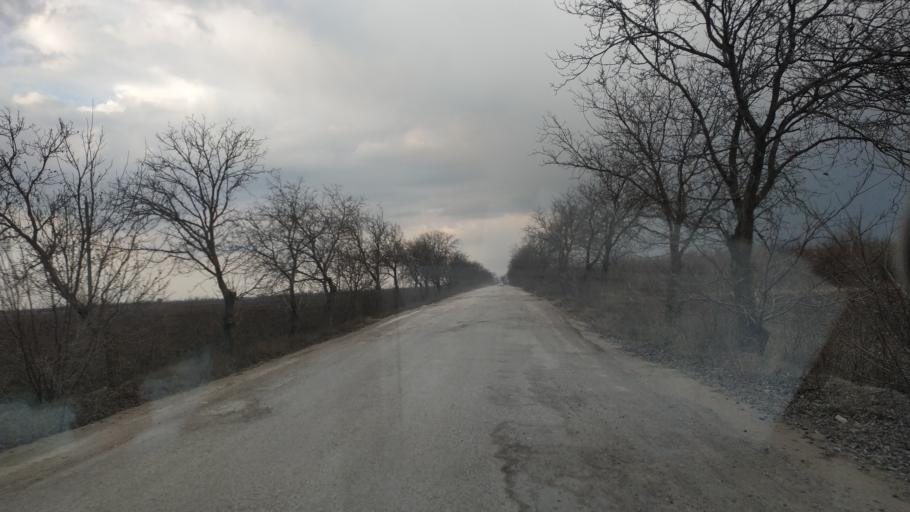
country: MD
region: Telenesti
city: Grigoriopol
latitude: 47.0502
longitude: 29.2936
